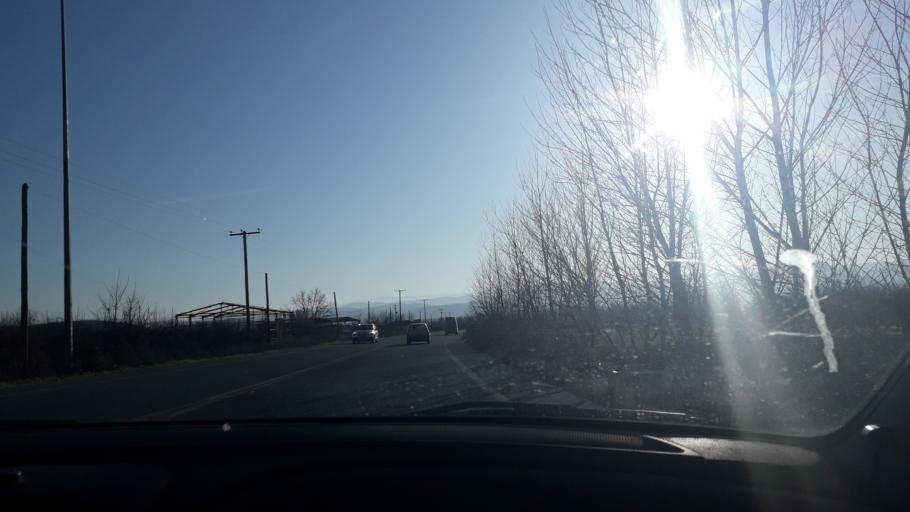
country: GR
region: Central Macedonia
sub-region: Nomos Pellis
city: Apsalos
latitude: 40.9266
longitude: 22.0834
